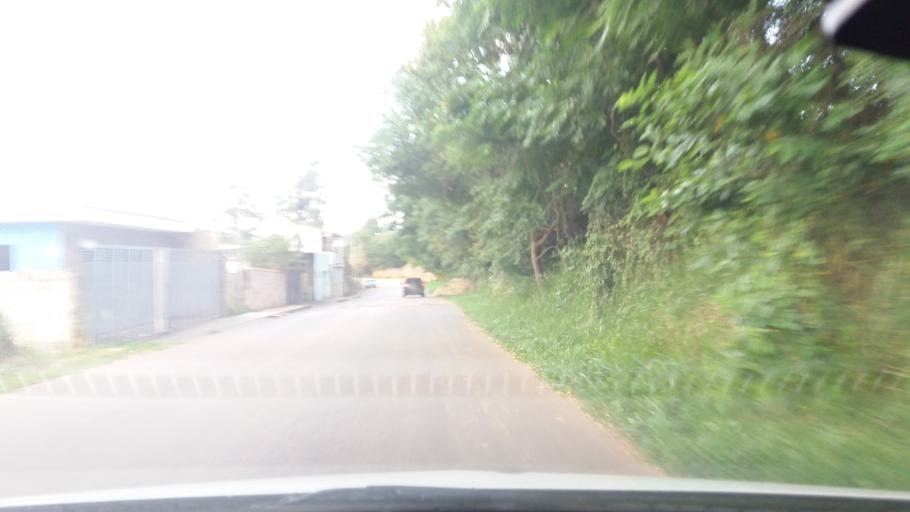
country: BR
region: Sao Paulo
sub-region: Bom Jesus Dos Perdoes
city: Bom Jesus dos Perdoes
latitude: -23.1612
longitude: -46.4755
